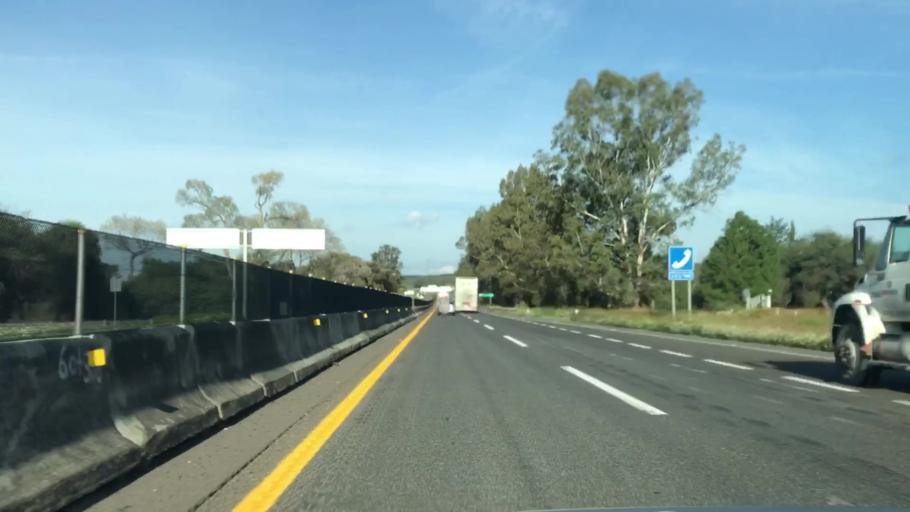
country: MX
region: Jalisco
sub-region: Lagos de Moreno
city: Cristeros [Fraccionamiento]
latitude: 21.3176
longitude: -102.0479
